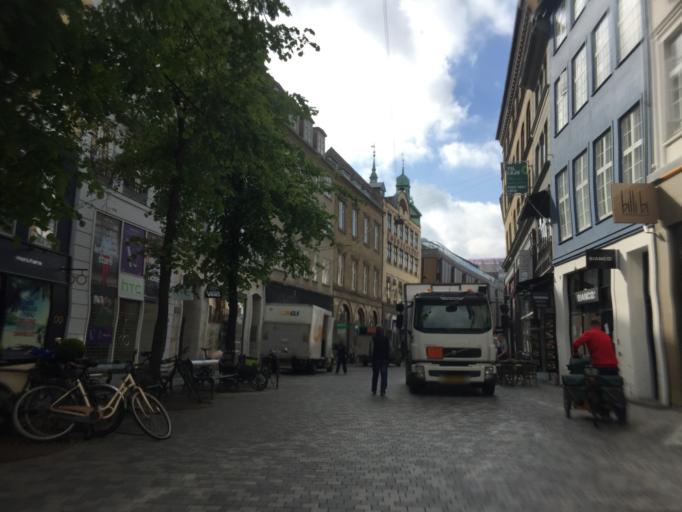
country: DK
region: Capital Region
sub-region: Kobenhavn
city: Copenhagen
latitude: 55.6804
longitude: 12.5785
